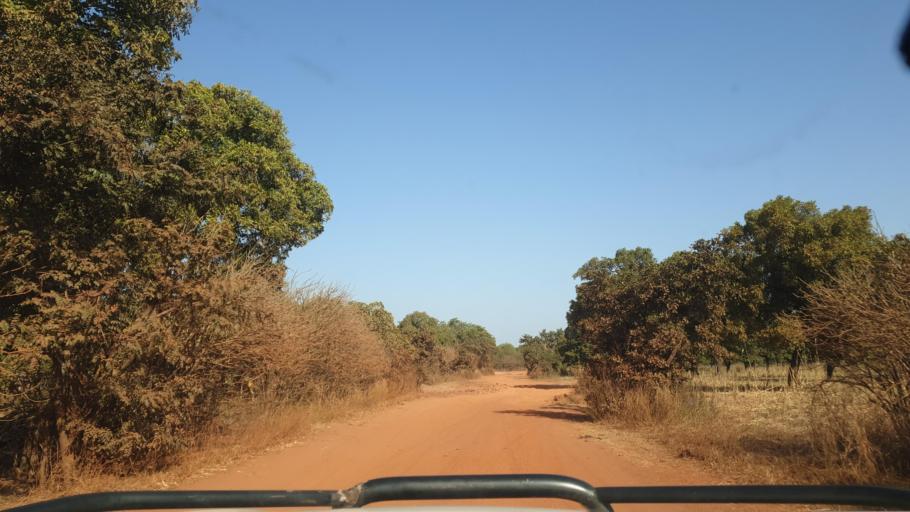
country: ML
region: Sikasso
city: Kolondieba
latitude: 11.7377
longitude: -6.8942
